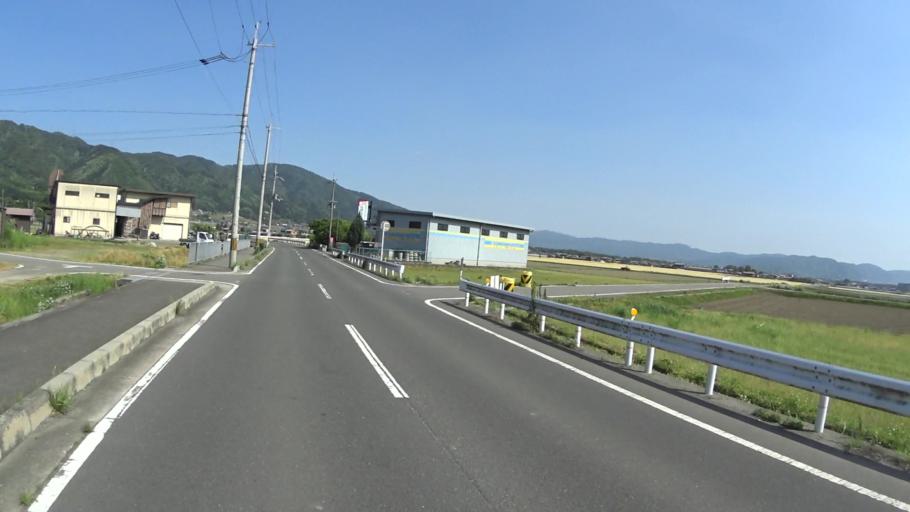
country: JP
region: Kyoto
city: Kameoka
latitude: 35.0654
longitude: 135.5592
